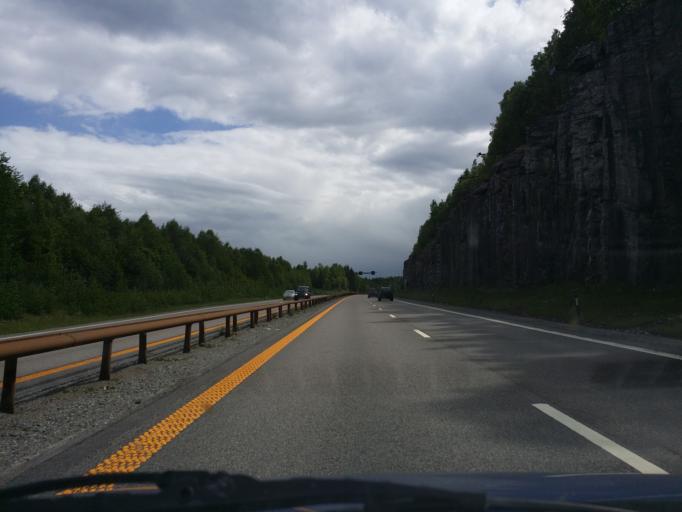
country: NO
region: Akershus
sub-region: Eidsvoll
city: Eidsvoll
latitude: 60.3554
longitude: 11.2069
